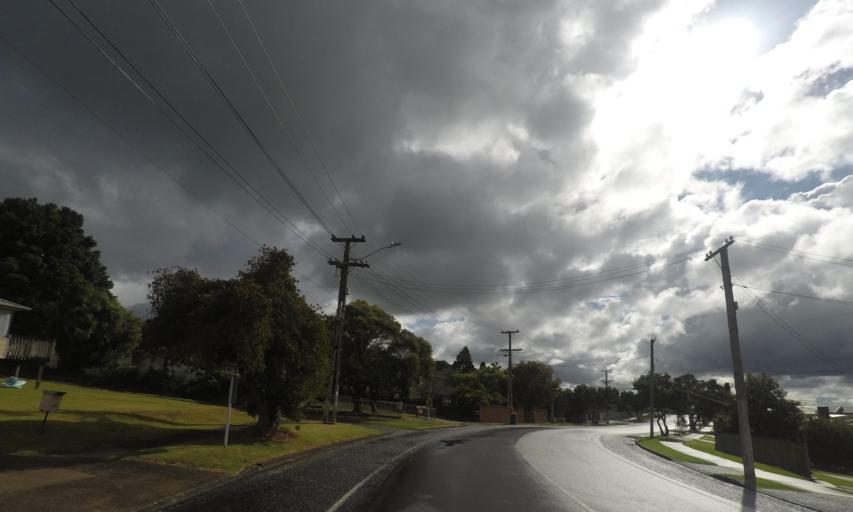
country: NZ
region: Auckland
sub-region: Auckland
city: Mangere
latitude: -36.9514
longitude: 174.7869
